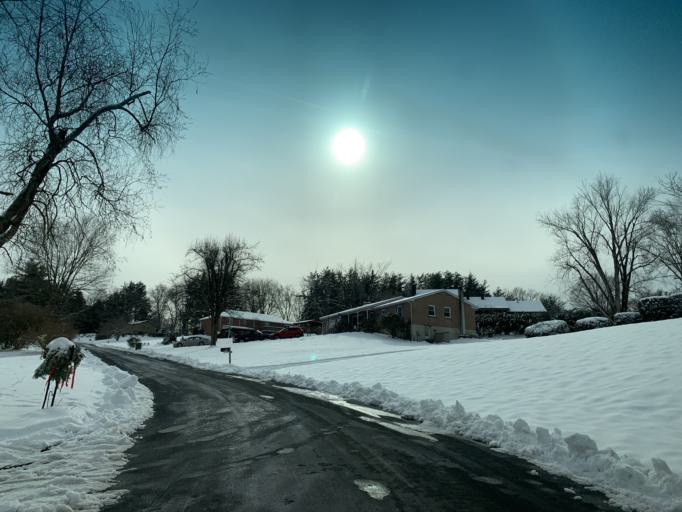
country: US
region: Maryland
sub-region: Harford County
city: Bel Air North
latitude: 39.6088
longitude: -76.3999
